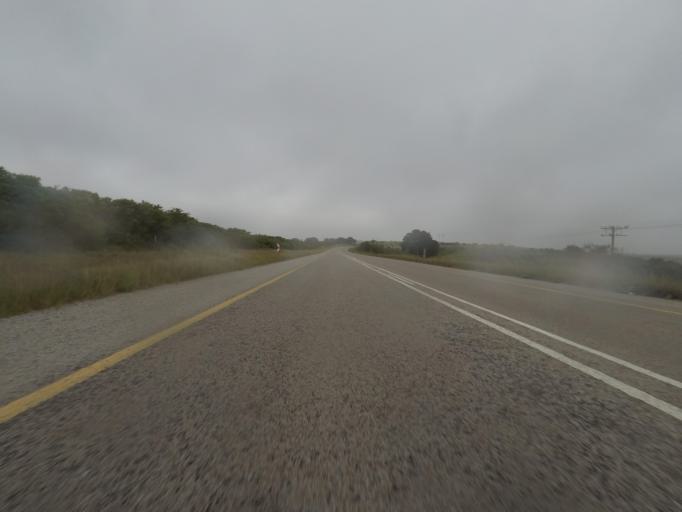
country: ZA
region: Eastern Cape
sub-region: Cacadu District Municipality
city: Grahamstown
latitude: -33.6427
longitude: 26.3652
